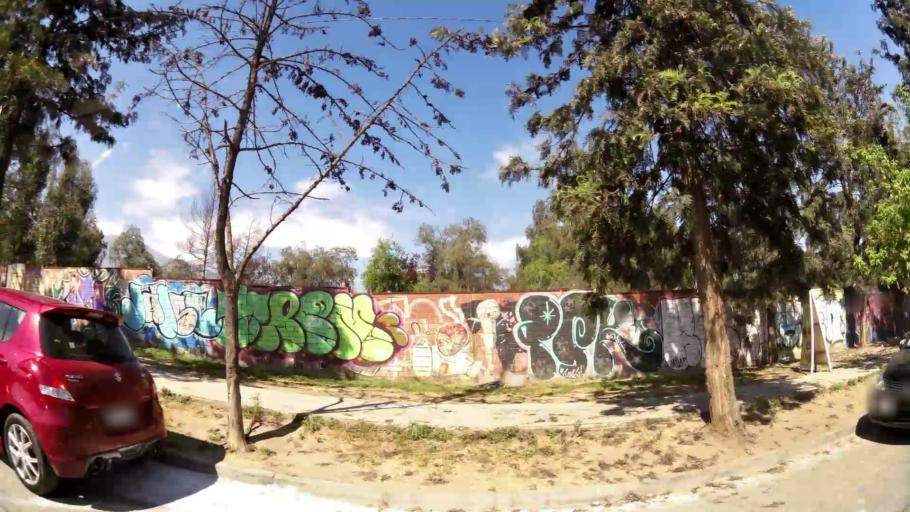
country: CL
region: Santiago Metropolitan
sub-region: Provincia de Santiago
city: Villa Presidente Frei, Nunoa, Santiago, Chile
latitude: -33.4585
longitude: -70.5403
